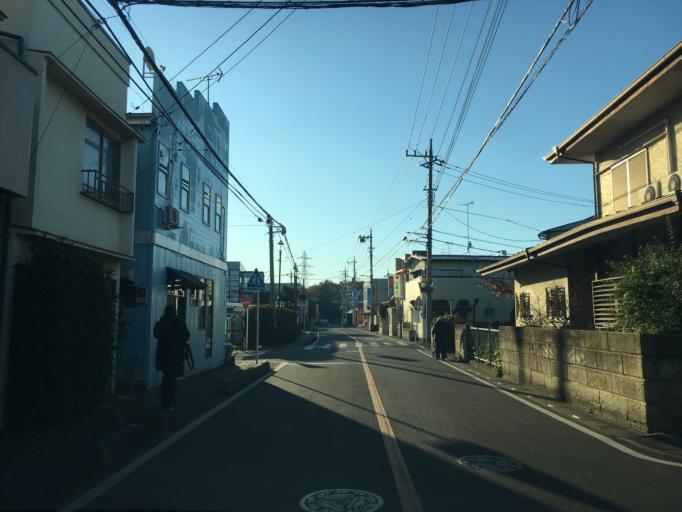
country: JP
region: Saitama
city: Tokorozawa
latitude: 35.8032
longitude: 139.4194
